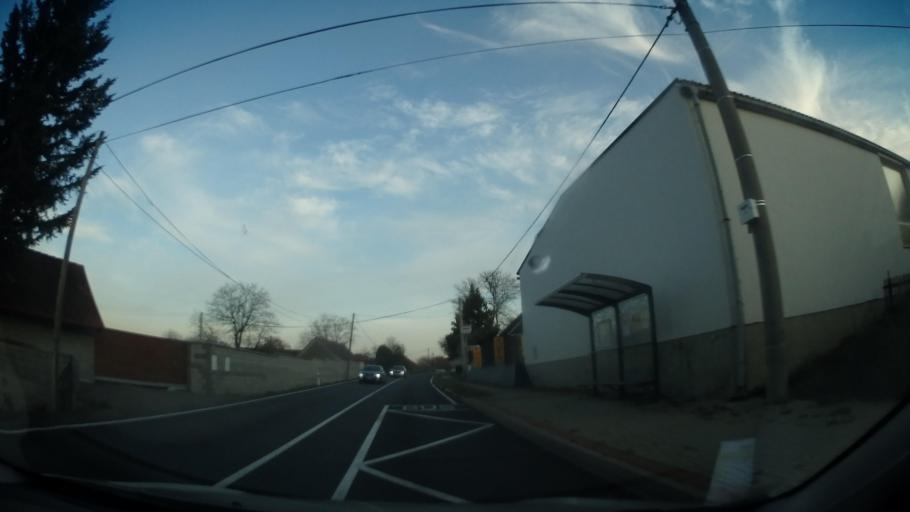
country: CZ
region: Central Bohemia
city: Vlasim
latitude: 49.6871
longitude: 14.9361
